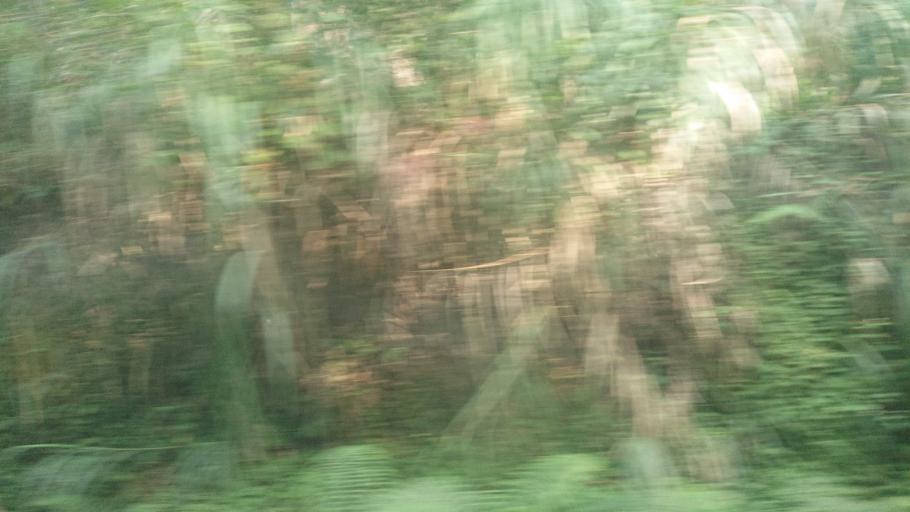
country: TW
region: Taiwan
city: Lugu
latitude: 23.5034
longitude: 120.7836
